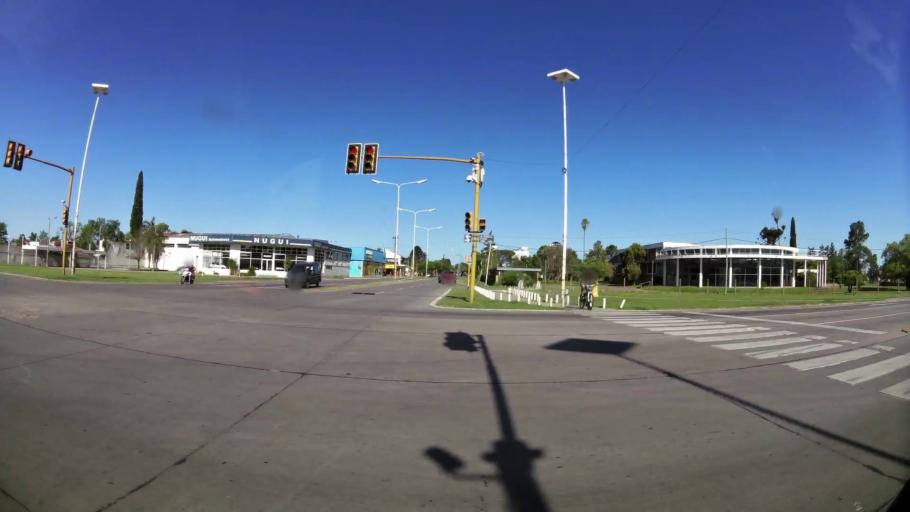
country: AR
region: Santa Fe
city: Rafaela
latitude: -31.2601
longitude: -61.5069
